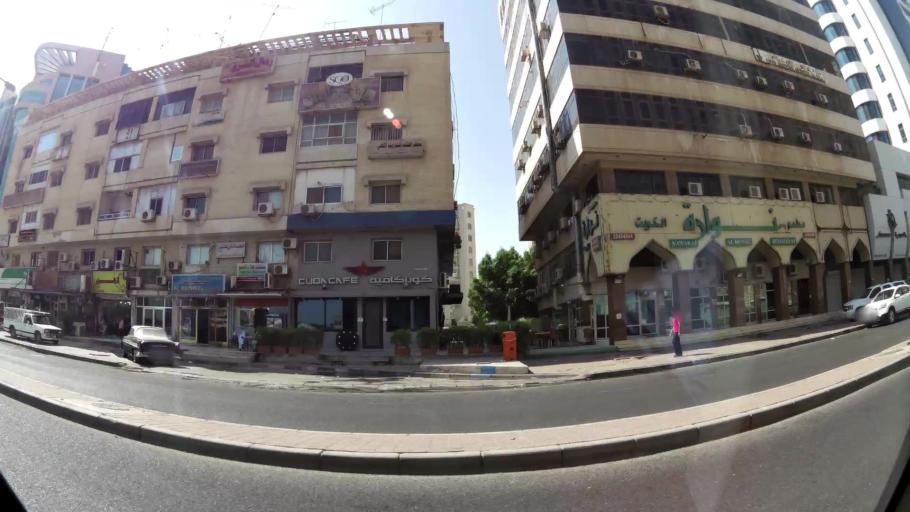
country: KW
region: Al Asimah
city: Kuwait City
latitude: 29.3822
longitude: 47.9902
